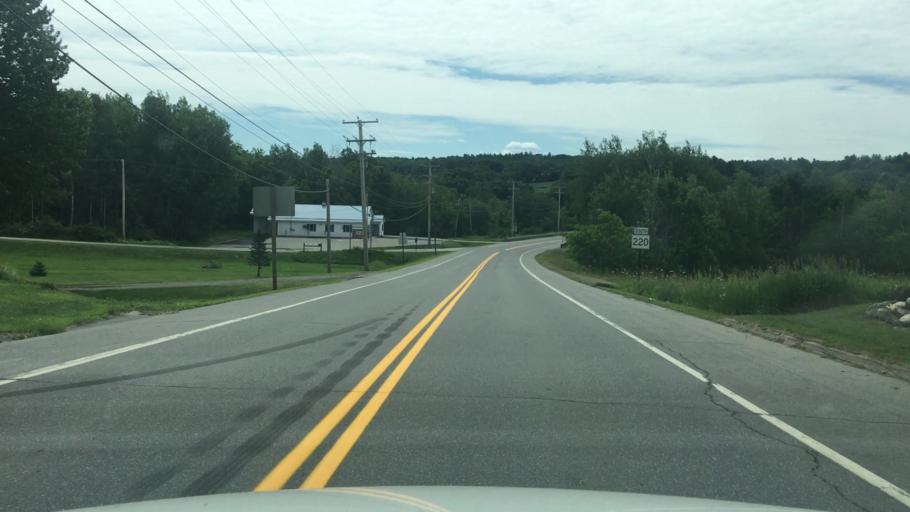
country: US
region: Maine
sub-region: Waldo County
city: Troy
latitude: 44.5778
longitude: -69.2773
